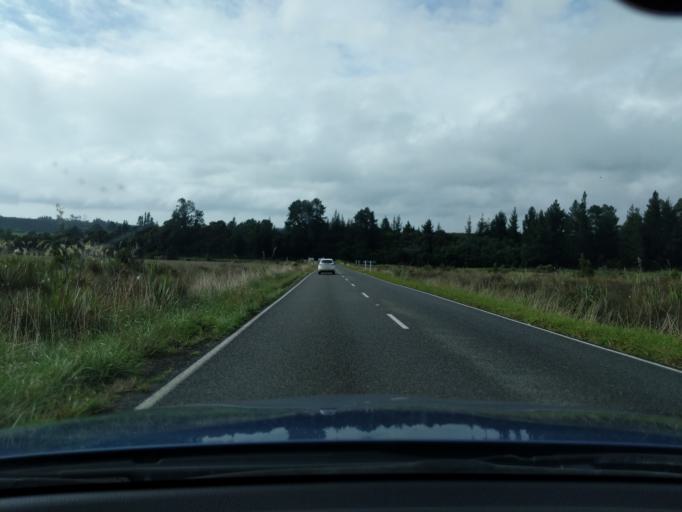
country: NZ
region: Tasman
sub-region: Tasman District
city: Takaka
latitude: -40.6797
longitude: 172.6651
